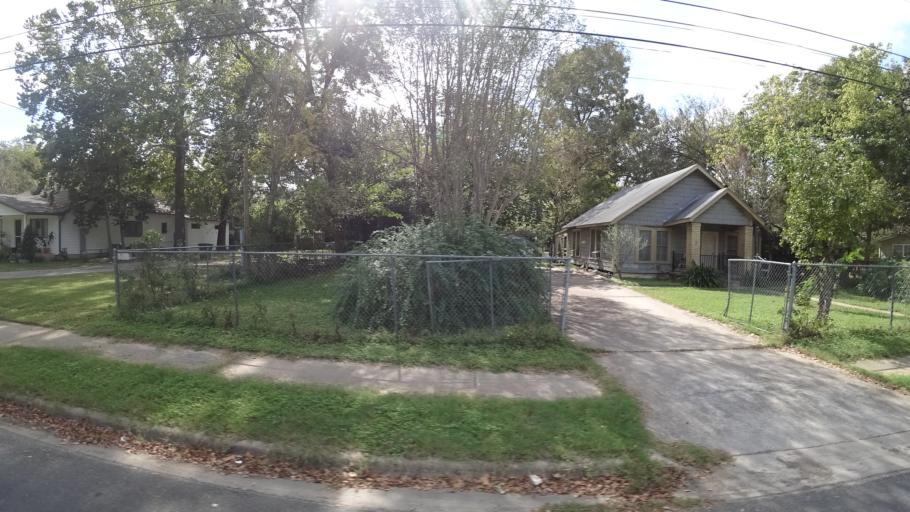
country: US
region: Texas
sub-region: Travis County
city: Austin
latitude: 30.2649
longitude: -97.7021
